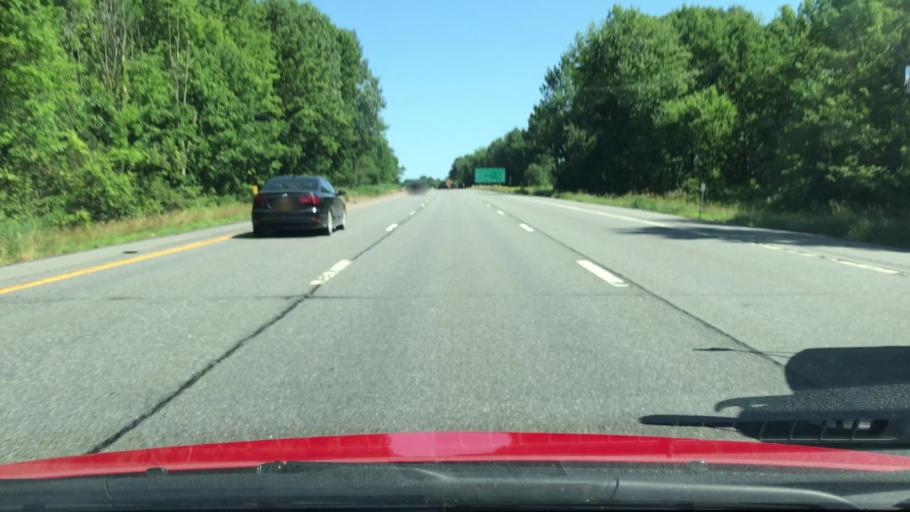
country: US
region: New York
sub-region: Warren County
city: West Glens Falls
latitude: 43.2087
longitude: -73.6938
